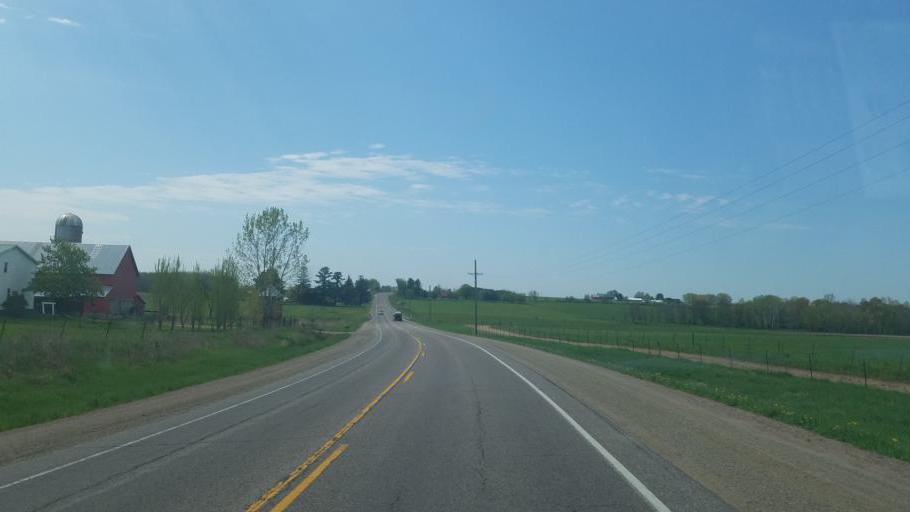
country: US
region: Wisconsin
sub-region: Marathon County
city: Spencer
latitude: 44.5938
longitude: -90.3763
